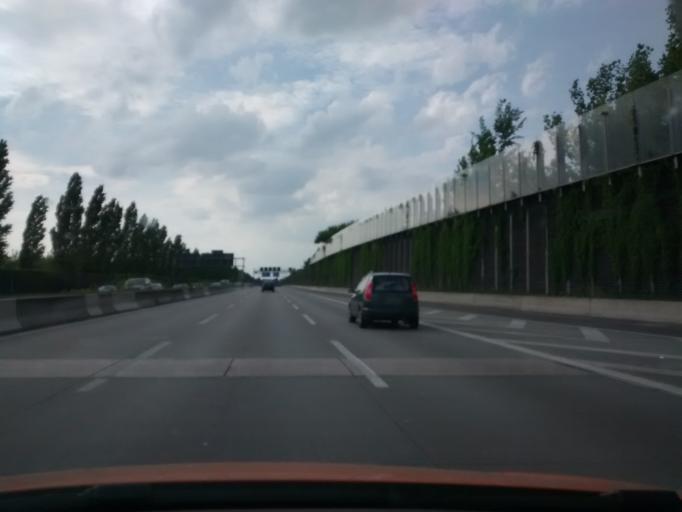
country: DE
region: Berlin
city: Buckow
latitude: 52.4441
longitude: 13.4769
